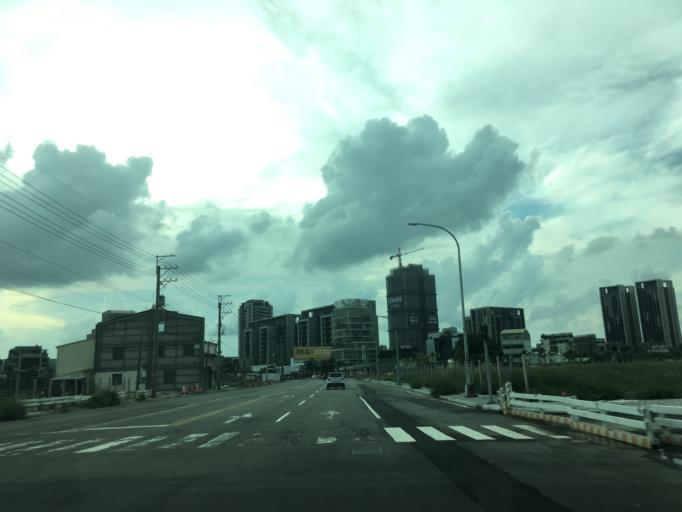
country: TW
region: Taiwan
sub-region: Taichung City
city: Taichung
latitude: 24.1389
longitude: 120.6307
